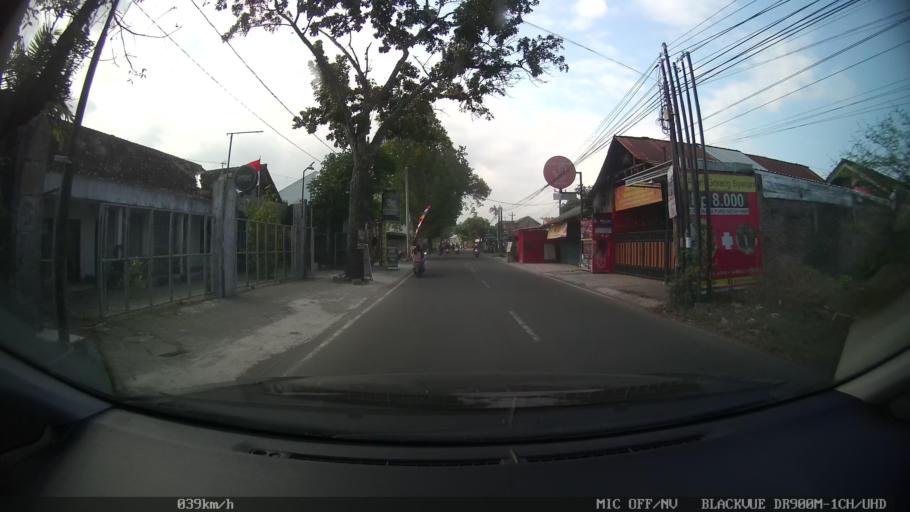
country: ID
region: Daerah Istimewa Yogyakarta
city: Sewon
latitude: -7.8499
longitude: 110.3905
